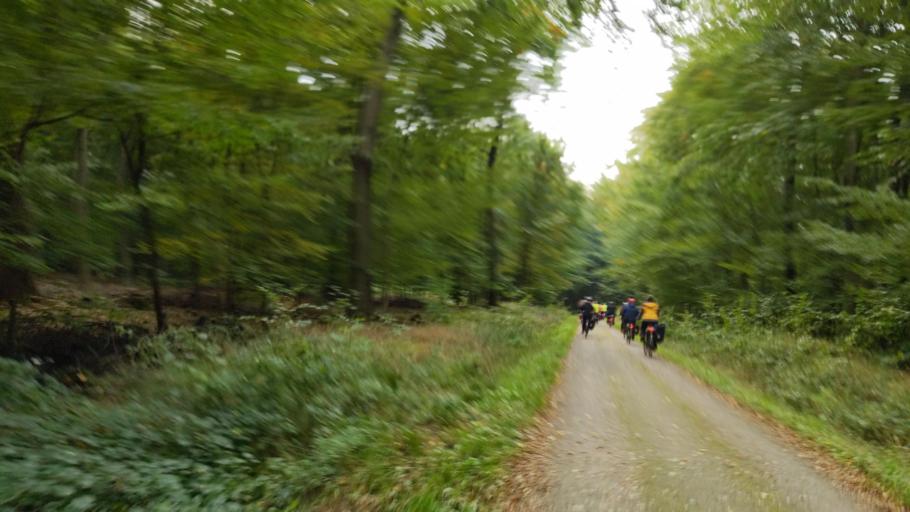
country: DE
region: Schleswig-Holstein
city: Meddewade
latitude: 53.8479
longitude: 10.4618
